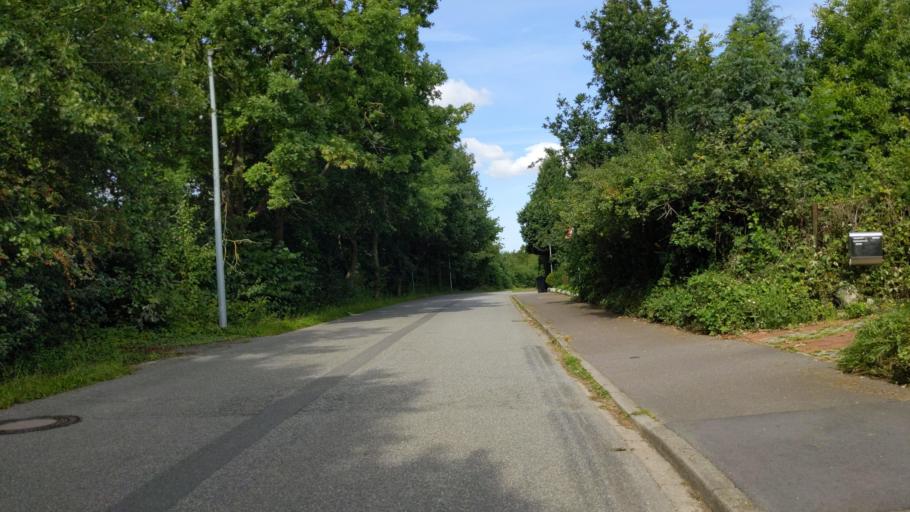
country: DE
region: Schleswig-Holstein
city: Schashagen
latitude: 54.1253
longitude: 10.8675
